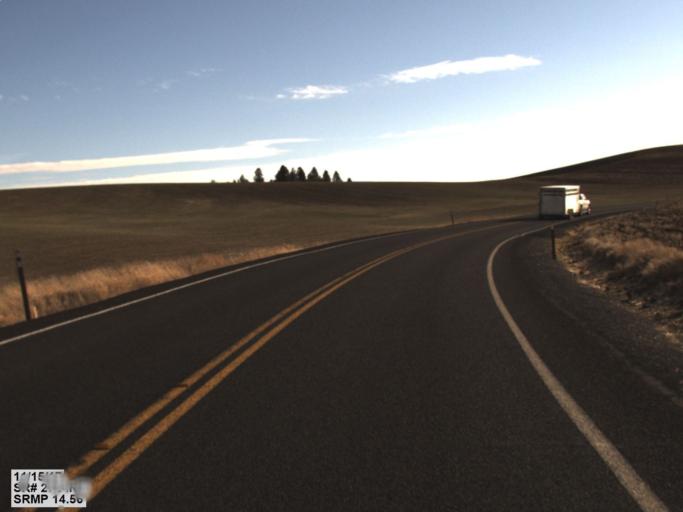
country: US
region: Washington
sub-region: Whitman County
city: Pullman
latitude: 46.9214
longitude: -117.1039
